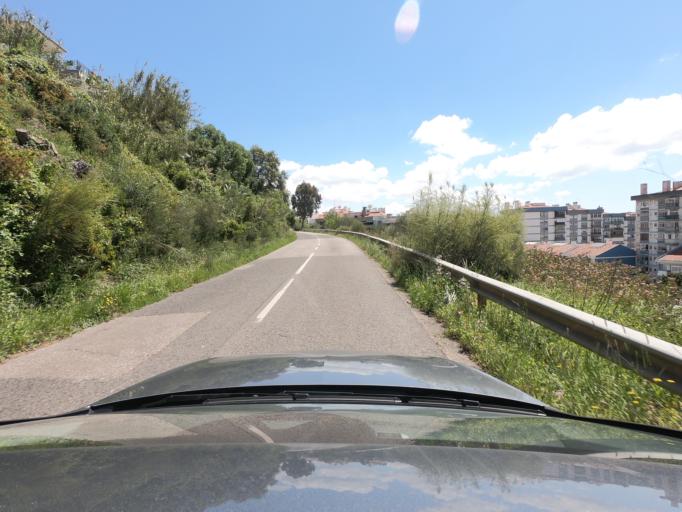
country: PT
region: Lisbon
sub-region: Oeiras
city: Carnaxide
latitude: 38.7288
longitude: -9.2410
